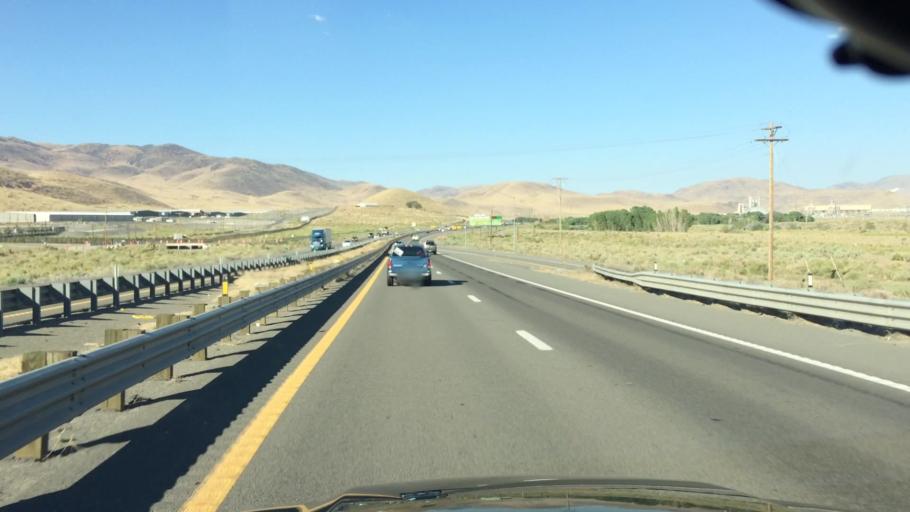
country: US
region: Nevada
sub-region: Washoe County
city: Spanish Springs
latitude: 39.5595
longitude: -119.5535
